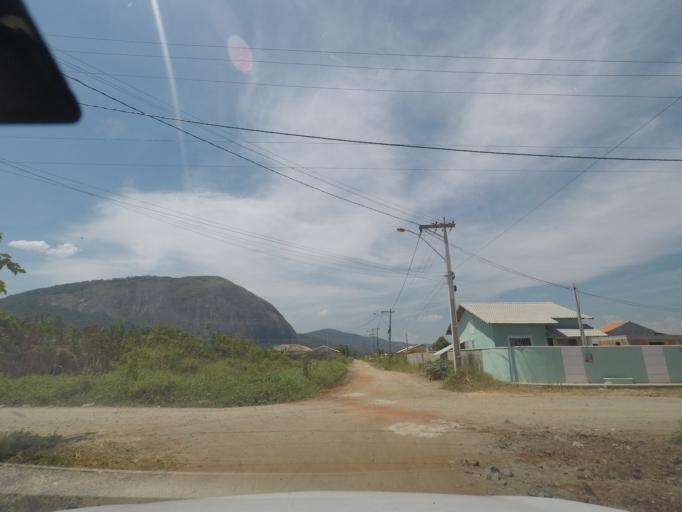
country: BR
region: Rio de Janeiro
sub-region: Marica
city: Marica
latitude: -22.9519
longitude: -42.9551
